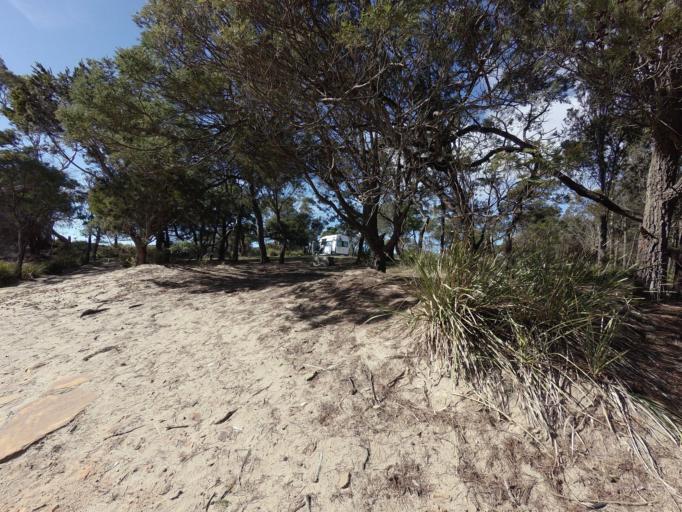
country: AU
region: Tasmania
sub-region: Clarence
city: Sandford
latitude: -42.9559
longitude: 147.7033
